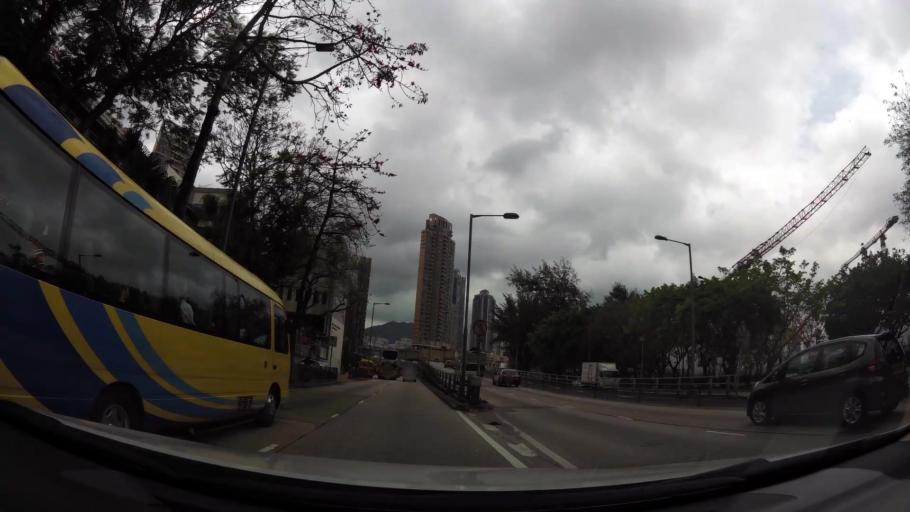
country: HK
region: Kowloon City
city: Kowloon
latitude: 22.3254
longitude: 114.1892
